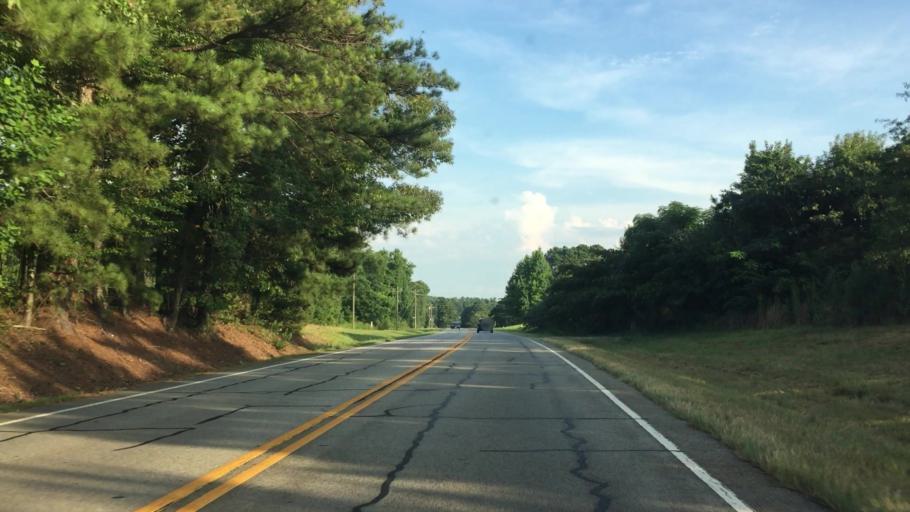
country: US
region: Georgia
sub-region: DeKalb County
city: Pine Mountain
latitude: 33.5941
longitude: -84.1528
